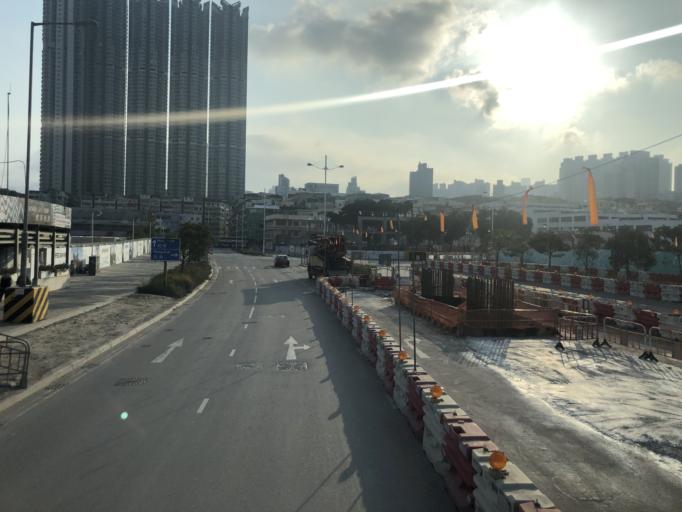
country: HK
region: Kowloon City
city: Kowloon
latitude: 22.3229
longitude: 114.1951
